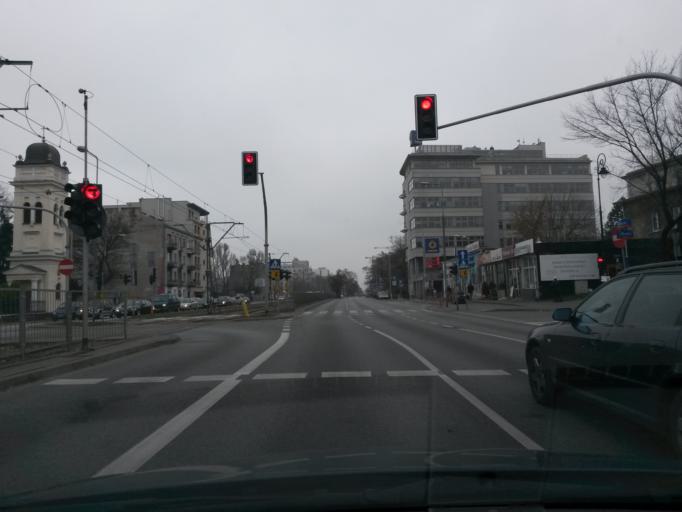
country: PL
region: Masovian Voivodeship
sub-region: Warszawa
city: Mokotow
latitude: 52.1995
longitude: 21.0237
